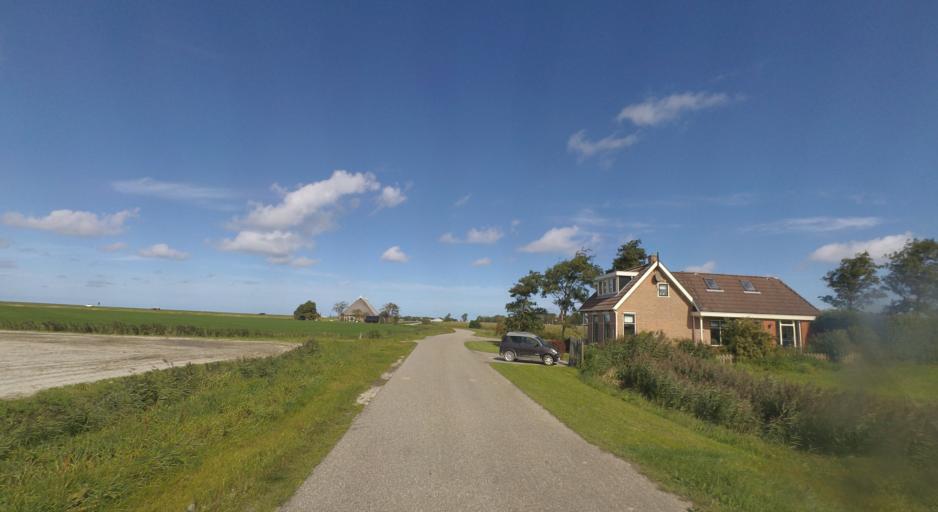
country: NL
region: Friesland
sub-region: Gemeente Dongeradeel
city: Holwerd
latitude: 53.3650
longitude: 5.8942
